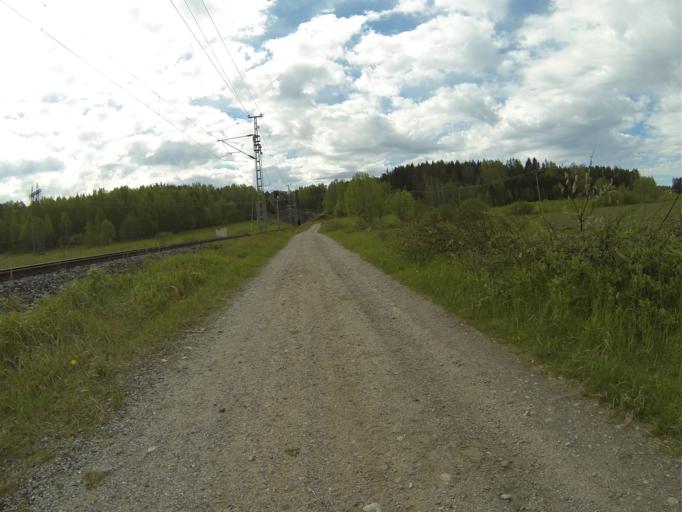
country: FI
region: Varsinais-Suomi
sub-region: Salo
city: Salo
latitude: 60.3585
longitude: 23.1176
